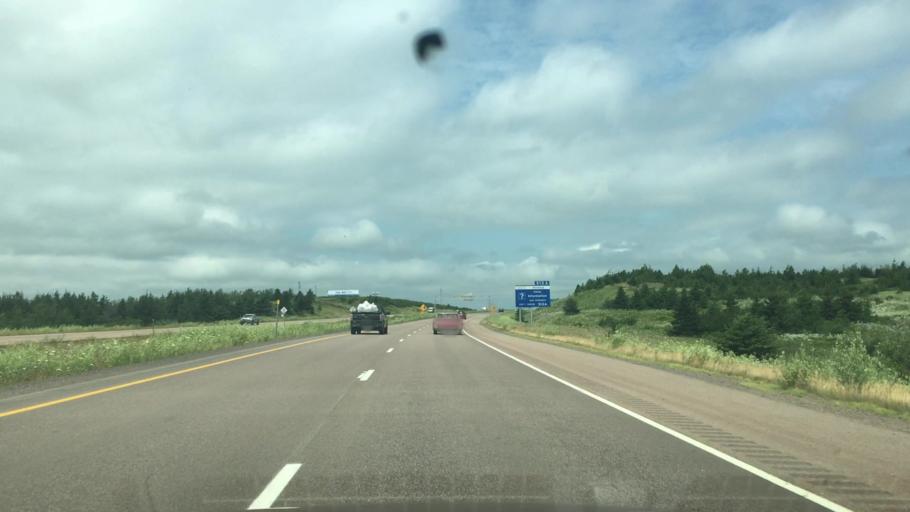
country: CA
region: Nova Scotia
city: Amherst
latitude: 45.8638
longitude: -64.2732
